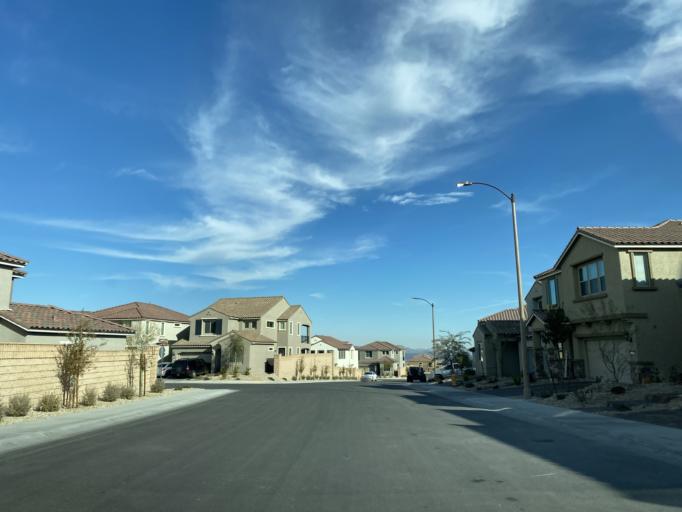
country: US
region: Nevada
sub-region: Clark County
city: Summerlin South
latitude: 36.3086
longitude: -115.3265
